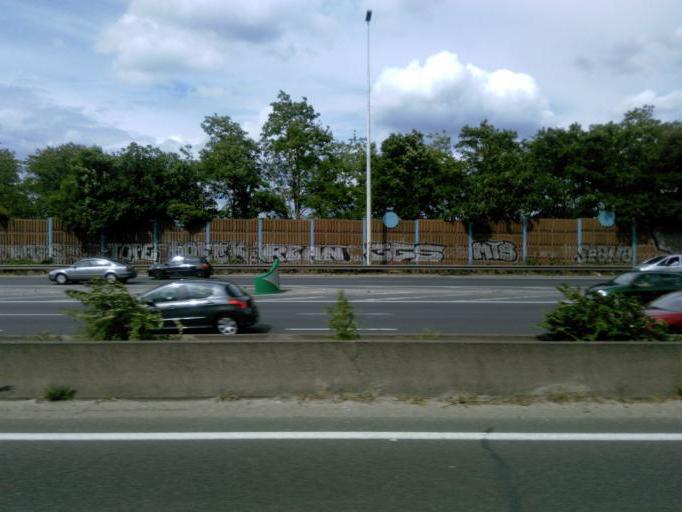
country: FR
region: Ile-de-France
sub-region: Departement du Val-d'Oise
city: Sannois
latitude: 48.9743
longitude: 2.2446
